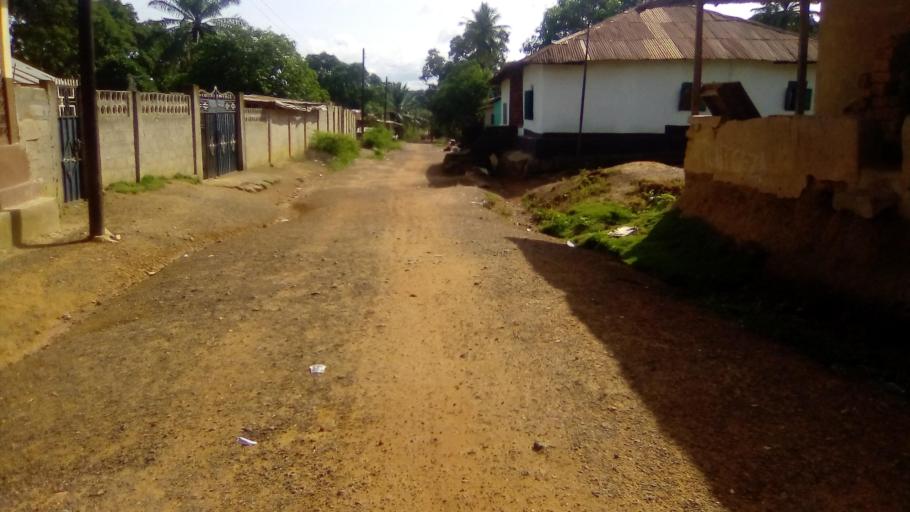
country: SL
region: Southern Province
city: Bo
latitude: 7.9733
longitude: -11.7321
